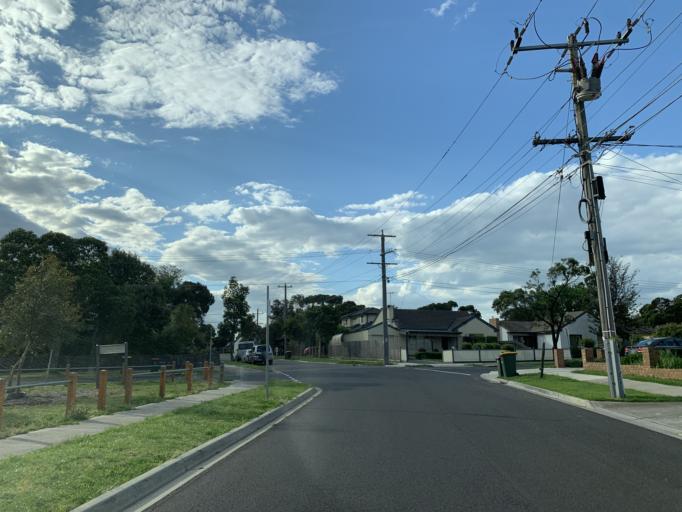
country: AU
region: Victoria
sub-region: Moonee Valley
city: Essendon West
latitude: -37.7572
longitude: 144.8554
